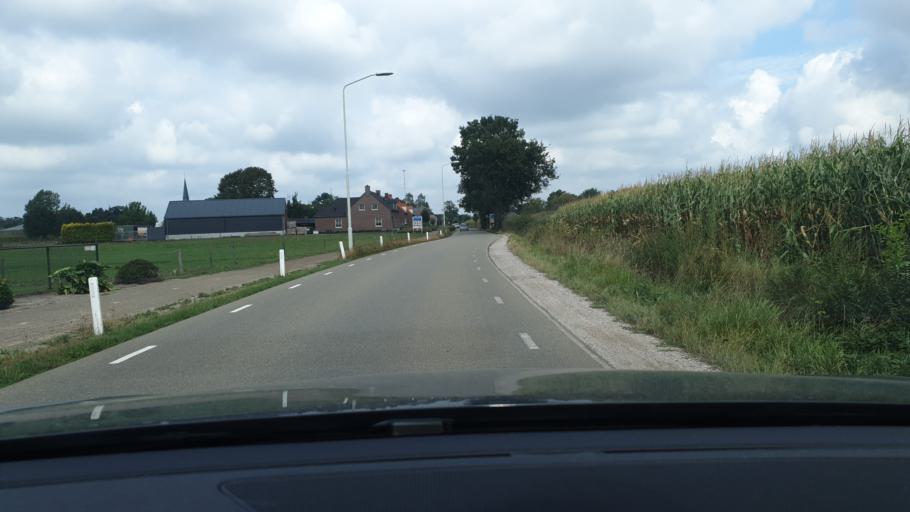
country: NL
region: North Brabant
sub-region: Gemeente Oirschot
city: Oostelbeers
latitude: 51.4668
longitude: 5.2743
